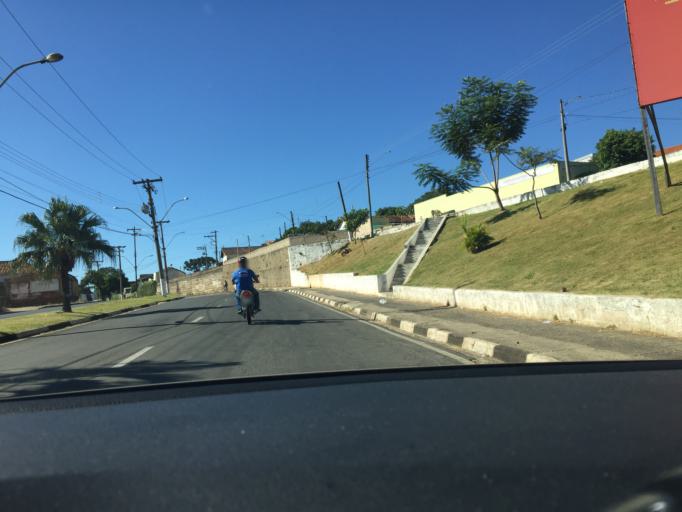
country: BR
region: Sao Paulo
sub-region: Santo Antonio Do Jardim
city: Espirito Santo do Pinhal
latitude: -22.1967
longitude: -46.7669
